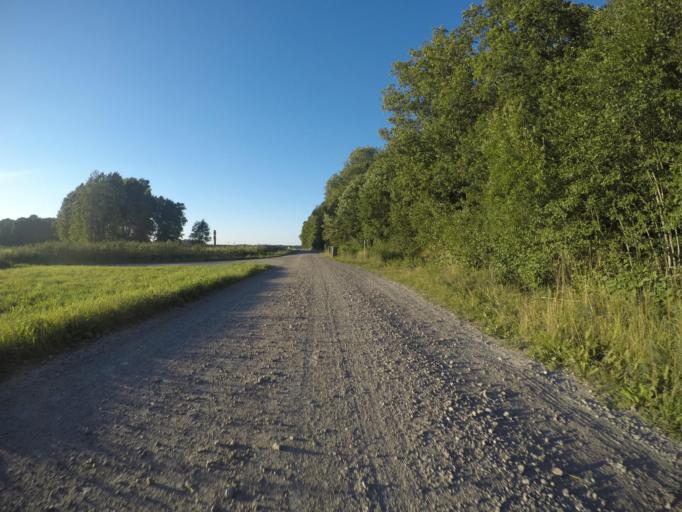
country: SE
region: Vaestmanland
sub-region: Vasteras
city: Vasteras
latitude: 59.5716
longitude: 16.6522
